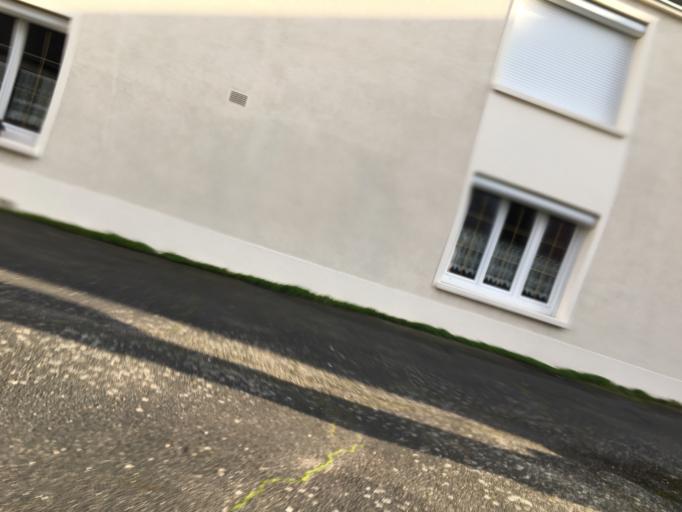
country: FR
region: Centre
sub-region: Departement du Loir-et-Cher
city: Mer
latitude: 47.7576
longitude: 1.5020
